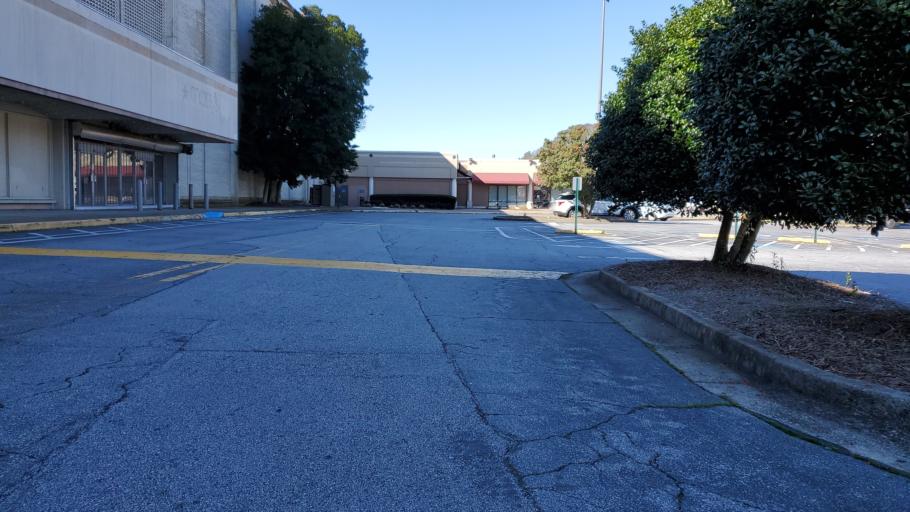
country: US
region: Georgia
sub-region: DeKalb County
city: Scottdale
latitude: 33.8090
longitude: -84.2760
